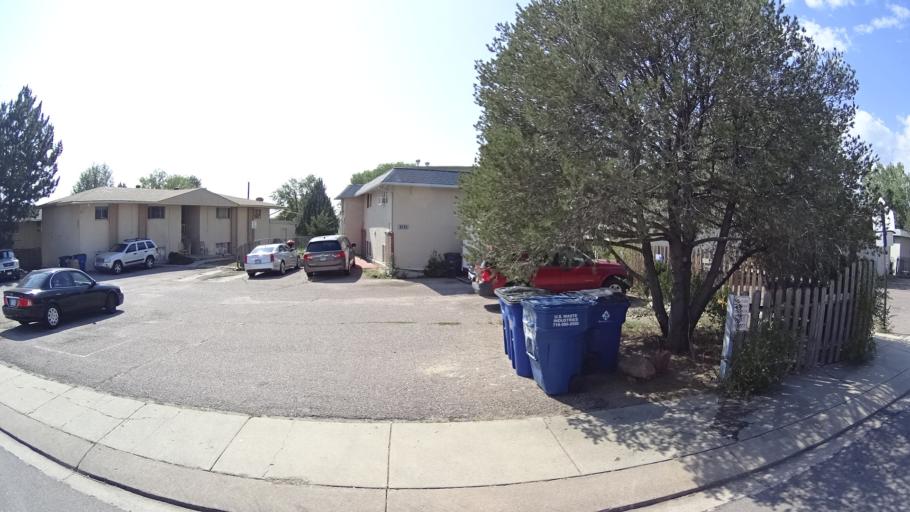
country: US
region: Colorado
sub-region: El Paso County
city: Colorado Springs
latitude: 38.8197
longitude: -104.7881
